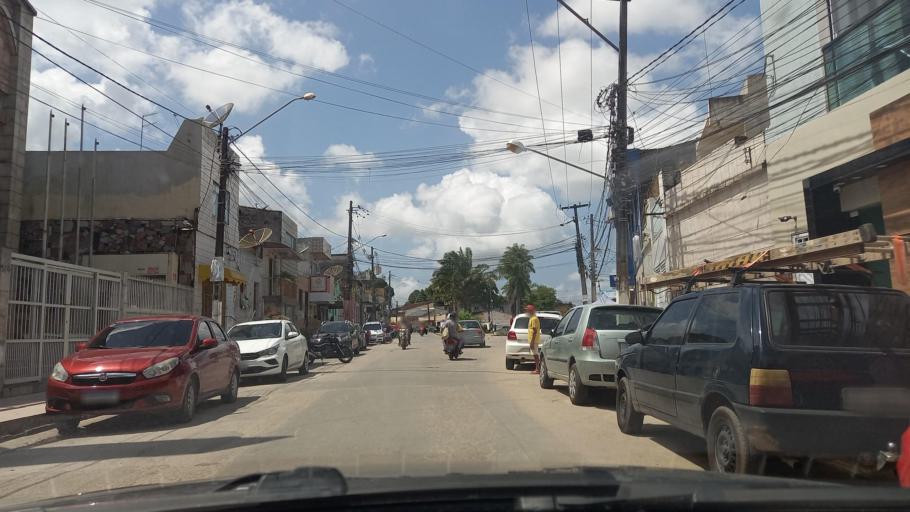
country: BR
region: Pernambuco
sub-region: Goiana
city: Goiana
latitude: -7.5620
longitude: -35.0028
